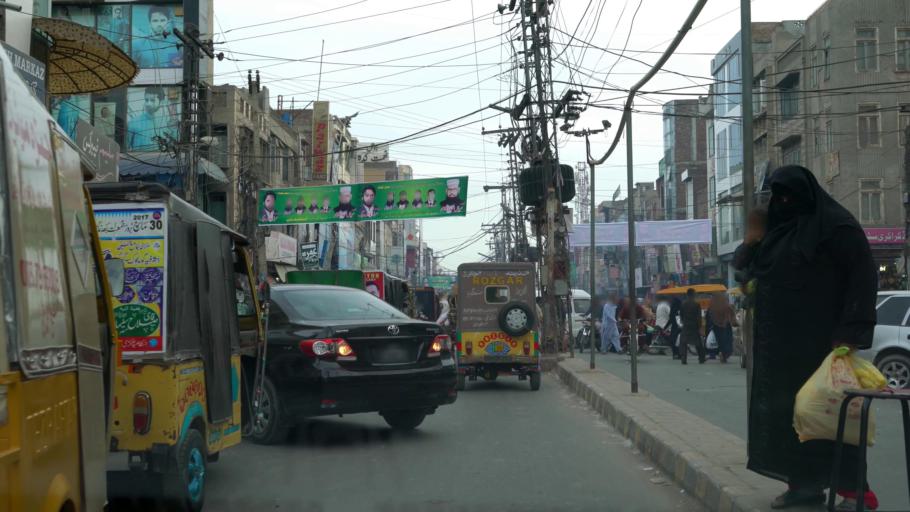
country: PK
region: Punjab
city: Sargodha
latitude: 32.0857
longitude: 72.6642
